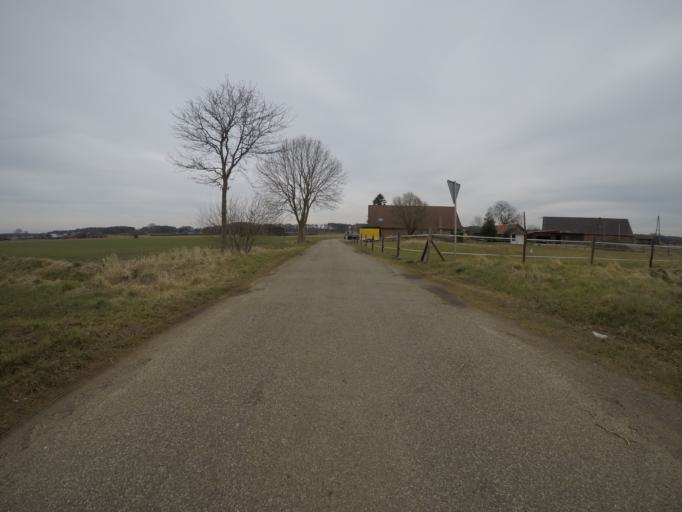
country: DE
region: North Rhine-Westphalia
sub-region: Regierungsbezirk Dusseldorf
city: Hamminkeln
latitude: 51.7436
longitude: 6.6337
